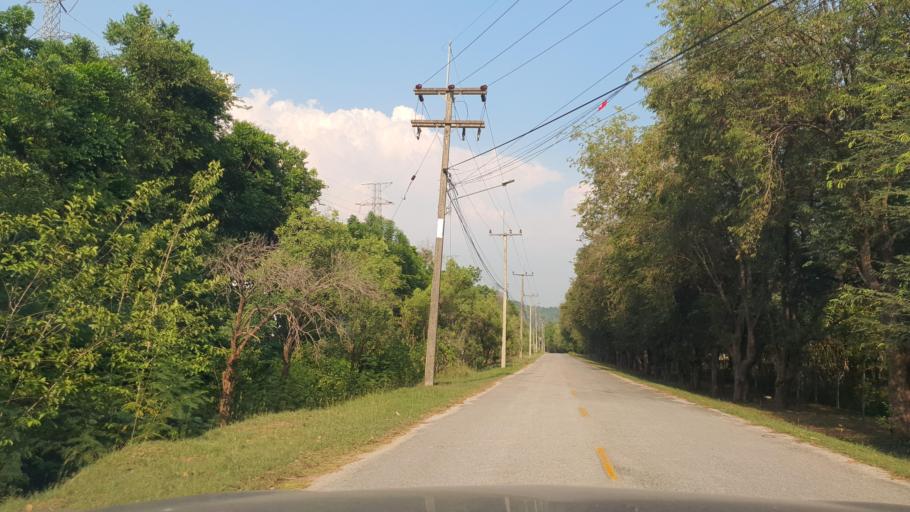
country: TH
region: Kanchanaburi
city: Sai Yok
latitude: 14.2255
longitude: 99.2261
